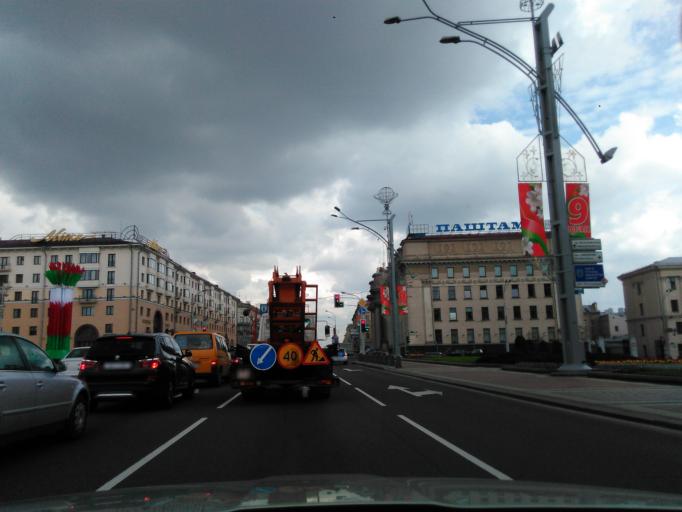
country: BY
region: Minsk
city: Minsk
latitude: 53.8956
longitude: 27.5493
